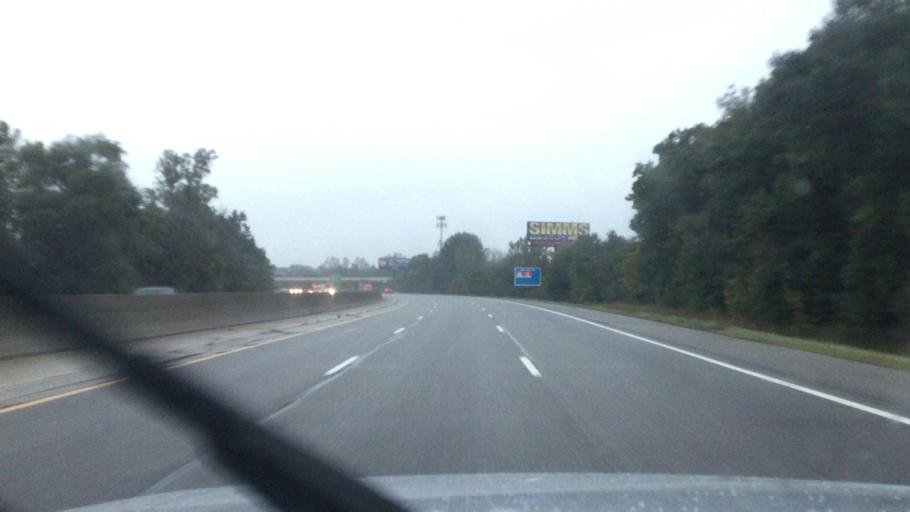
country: US
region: Michigan
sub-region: Genesee County
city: Flint
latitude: 43.0425
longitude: -83.7537
